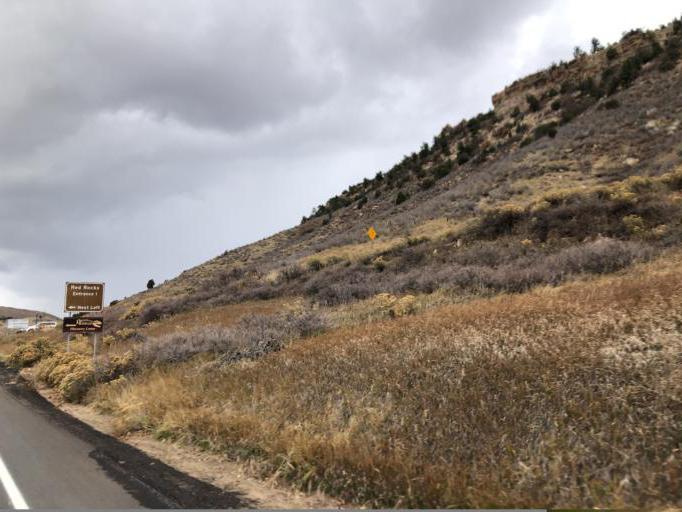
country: US
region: Colorado
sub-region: Jefferson County
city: West Pleasant View
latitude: 39.6789
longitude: -105.1962
